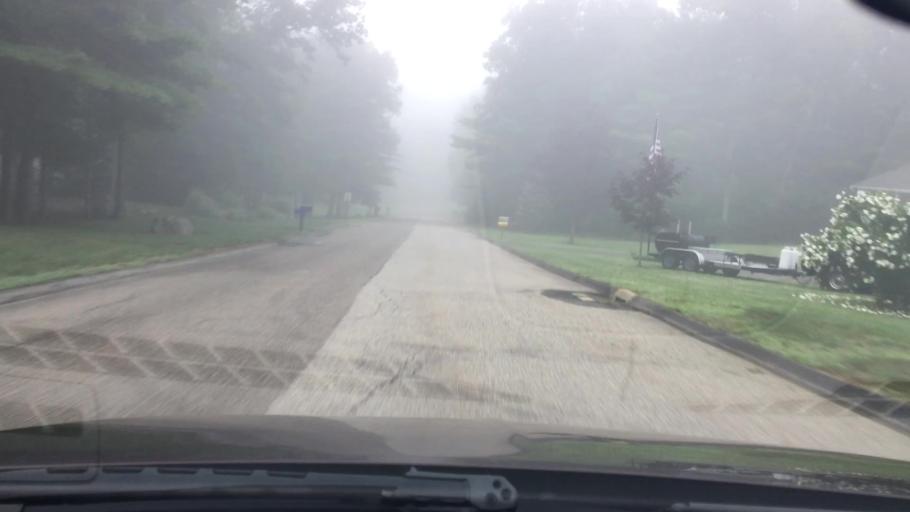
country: US
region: Connecticut
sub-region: Tolland County
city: Stafford
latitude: 41.9844
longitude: -72.3246
